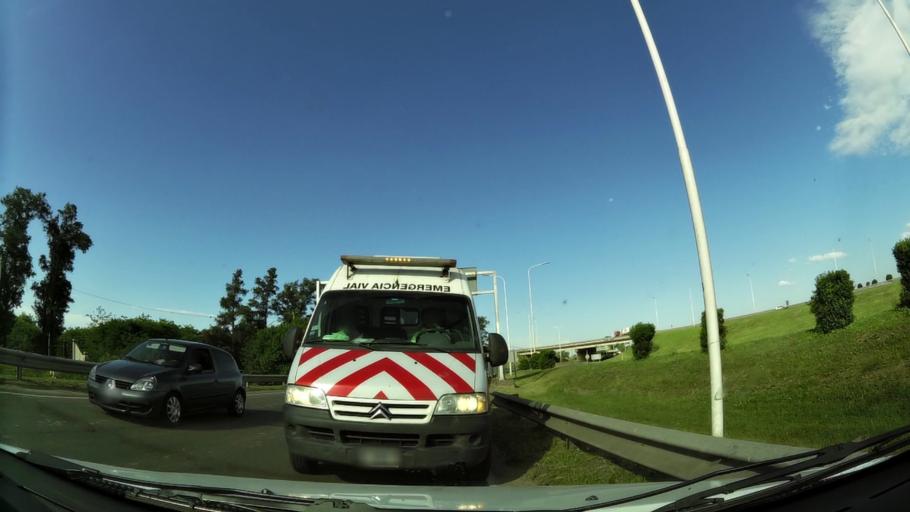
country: AR
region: Buenos Aires
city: Hurlingham
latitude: -34.5635
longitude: -58.6305
